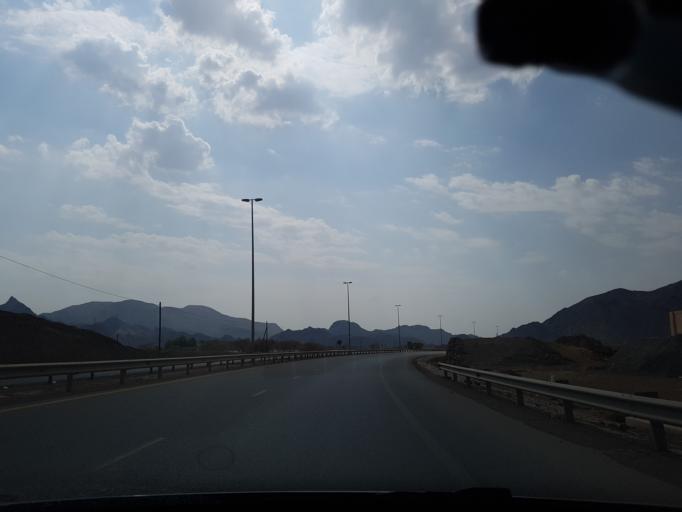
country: AE
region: Al Fujayrah
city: Dibba Al-Fujairah
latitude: 25.5000
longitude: 56.0711
